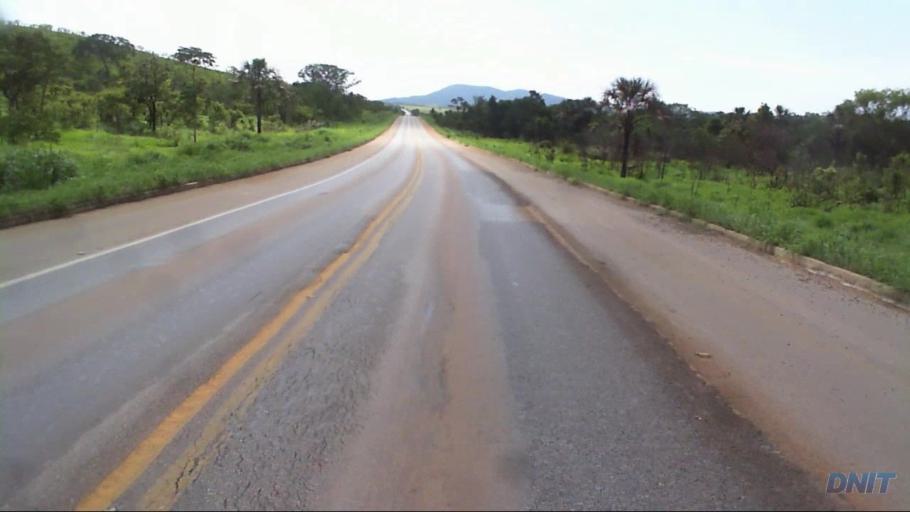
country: BR
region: Goias
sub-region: Barro Alto
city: Barro Alto
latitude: -15.1774
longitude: -48.7928
